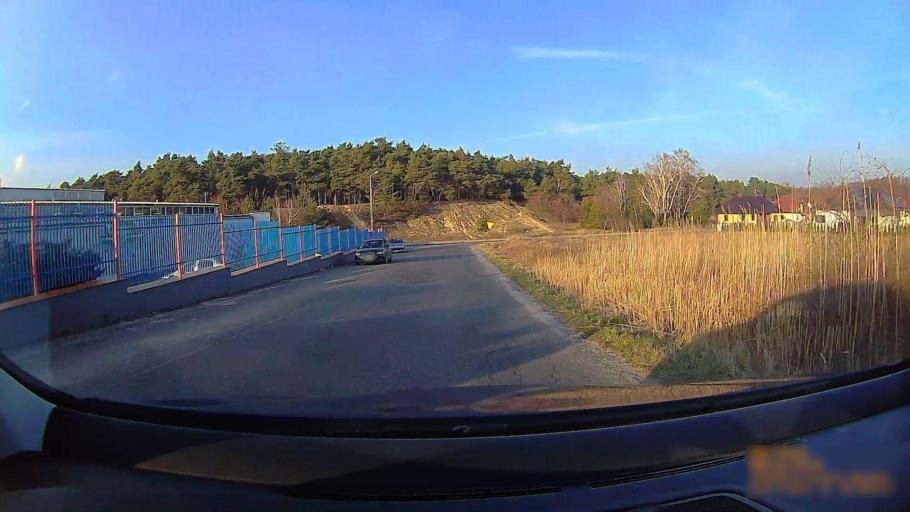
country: PL
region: Greater Poland Voivodeship
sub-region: Konin
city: Konin
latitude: 52.1962
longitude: 18.3152
